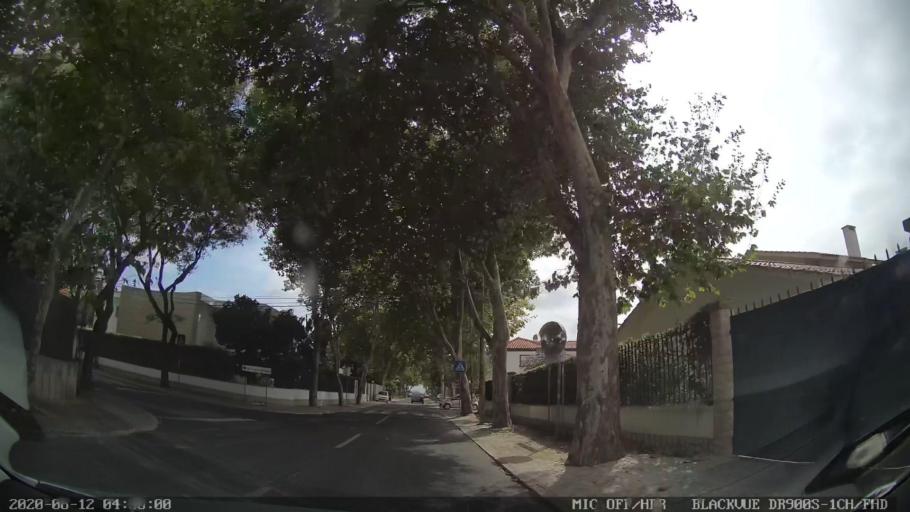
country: PT
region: Lisbon
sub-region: Cascais
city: Estoril
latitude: 38.6988
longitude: -9.3784
